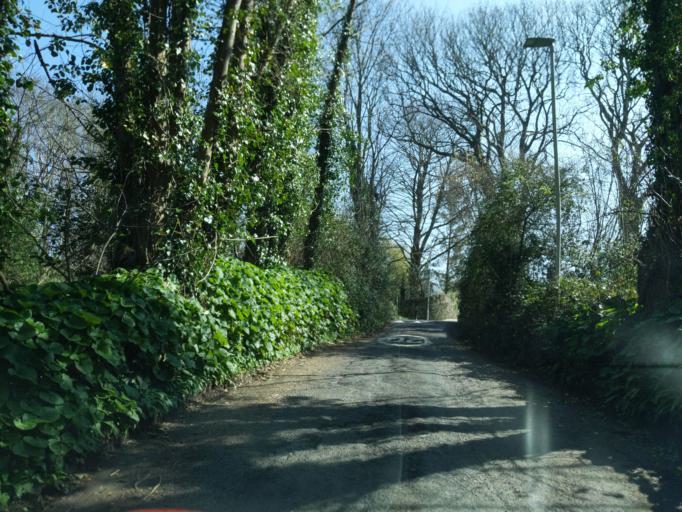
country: GB
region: England
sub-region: Devon
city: Plympton
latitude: 50.3844
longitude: -4.0490
